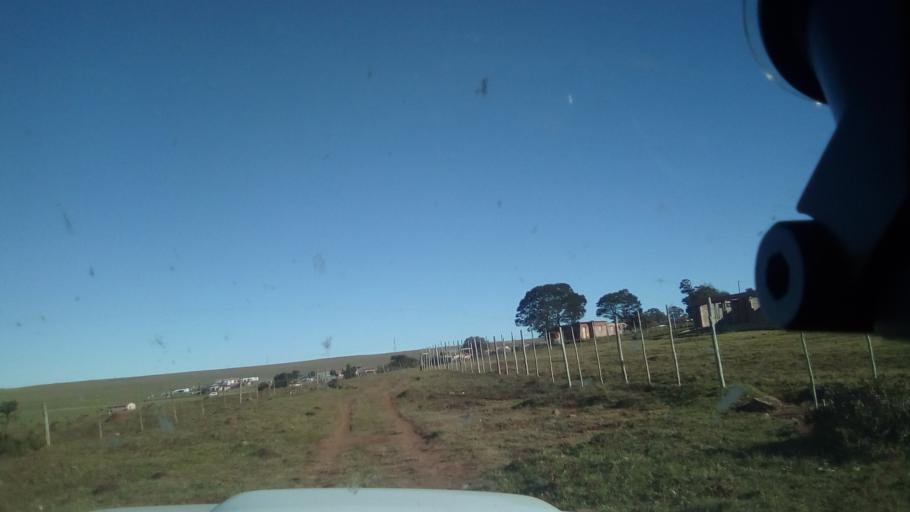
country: ZA
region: Eastern Cape
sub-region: Buffalo City Metropolitan Municipality
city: Bhisho
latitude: -32.9474
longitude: 27.2965
